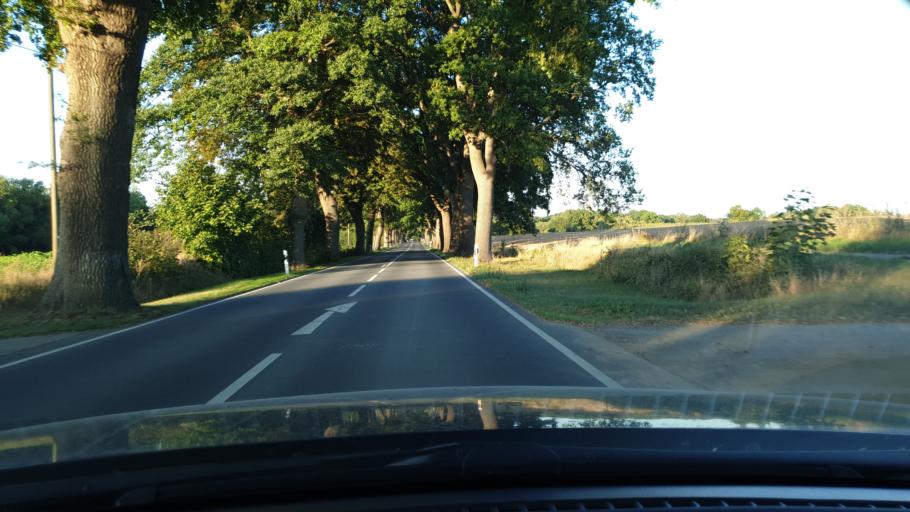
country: DE
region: Mecklenburg-Vorpommern
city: Wittenburg
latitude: 53.5860
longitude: 11.1136
